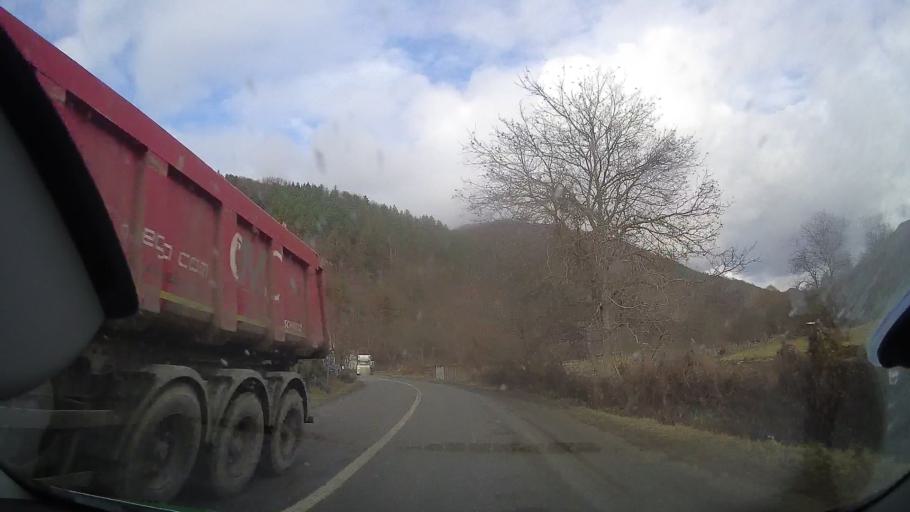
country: RO
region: Alba
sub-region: Comuna Ocolis
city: Ocolis
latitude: 46.4788
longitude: 23.5078
